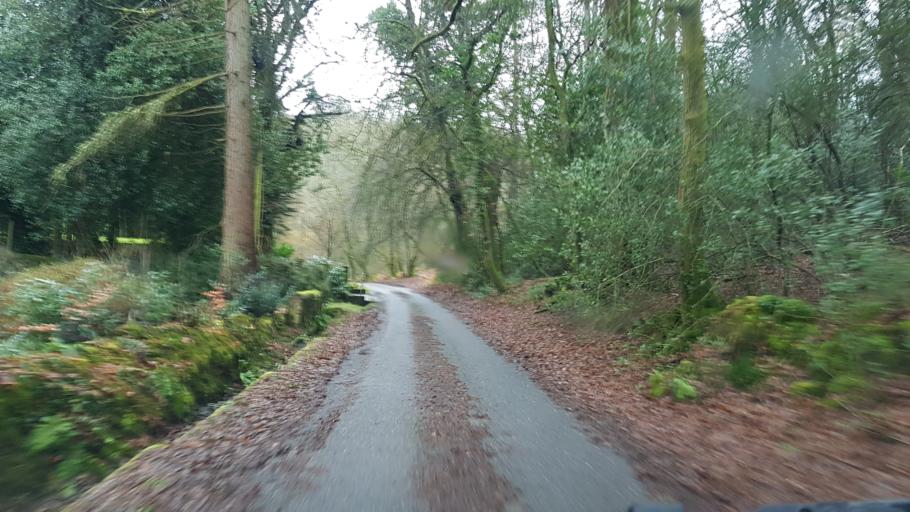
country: GB
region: England
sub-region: Surrey
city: Churt
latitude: 51.1044
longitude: -0.7705
